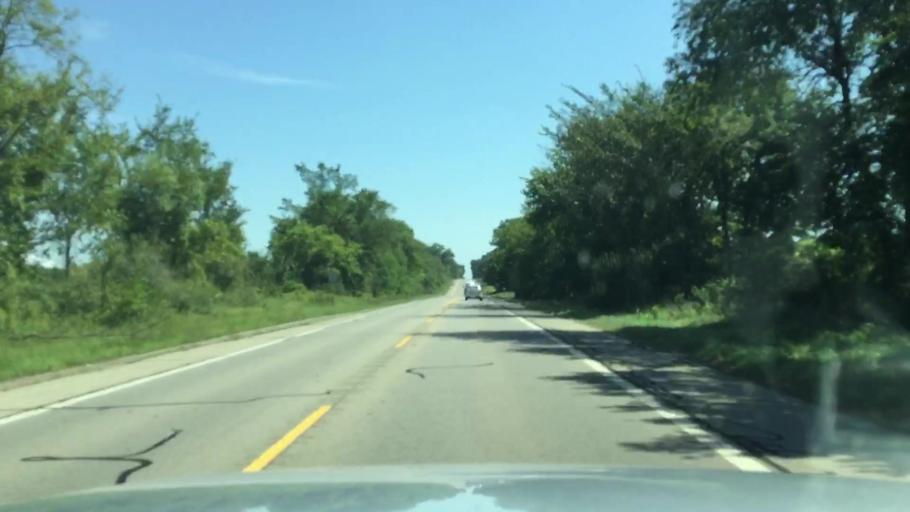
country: US
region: Michigan
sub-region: Washtenaw County
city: Manchester
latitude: 42.0727
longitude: -84.0572
